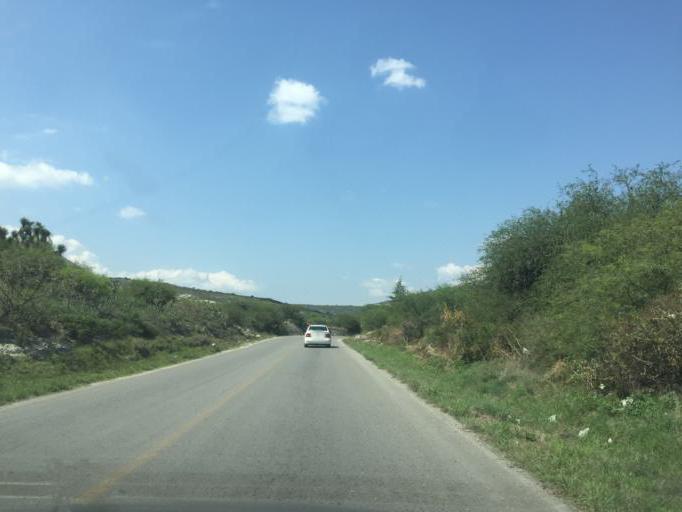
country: MX
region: Hidalgo
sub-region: Cardonal
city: Pozuelos
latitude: 20.5985
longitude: -99.1161
